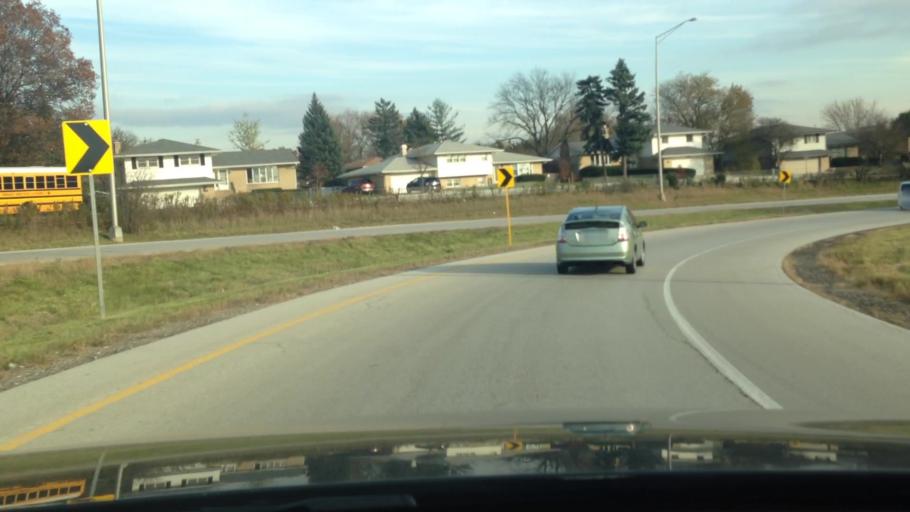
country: US
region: Illinois
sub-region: Cook County
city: Rolling Meadows
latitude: 42.0643
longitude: -88.0256
